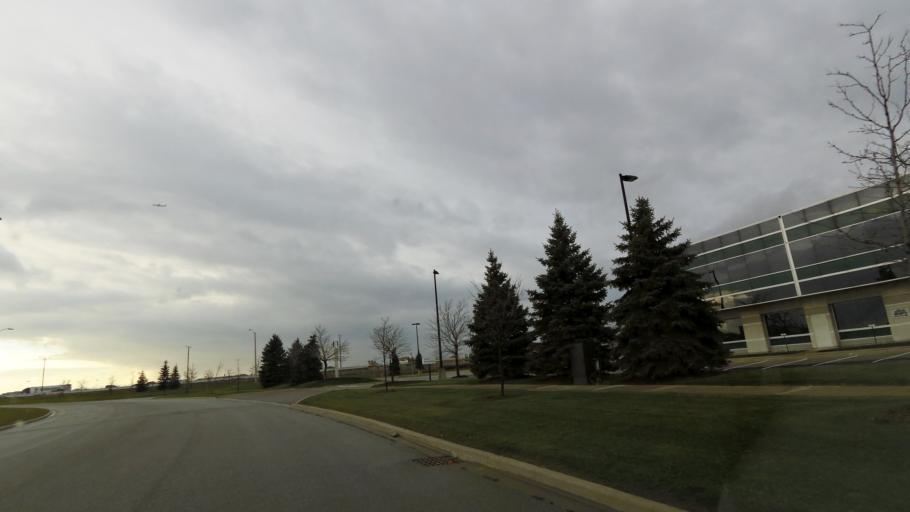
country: CA
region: Ontario
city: Mississauga
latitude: 43.6210
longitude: -79.7016
